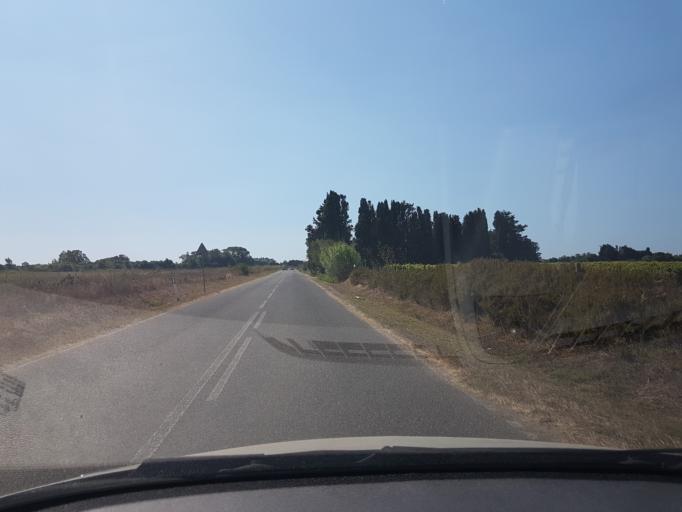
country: IT
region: Sardinia
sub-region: Provincia di Oristano
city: Riola Sardo
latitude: 39.9986
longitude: 8.4980
